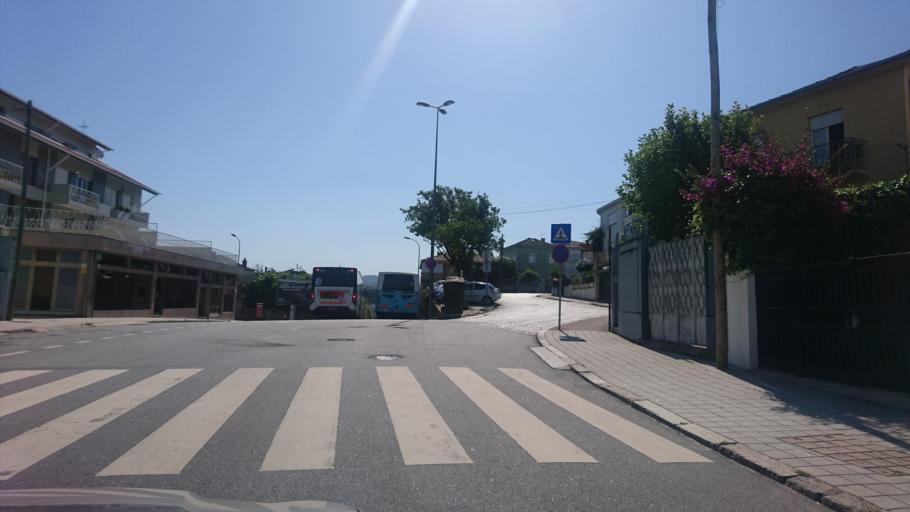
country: PT
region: Porto
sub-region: Gondomar
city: Rio Tinto
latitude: 41.1663
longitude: -8.5690
